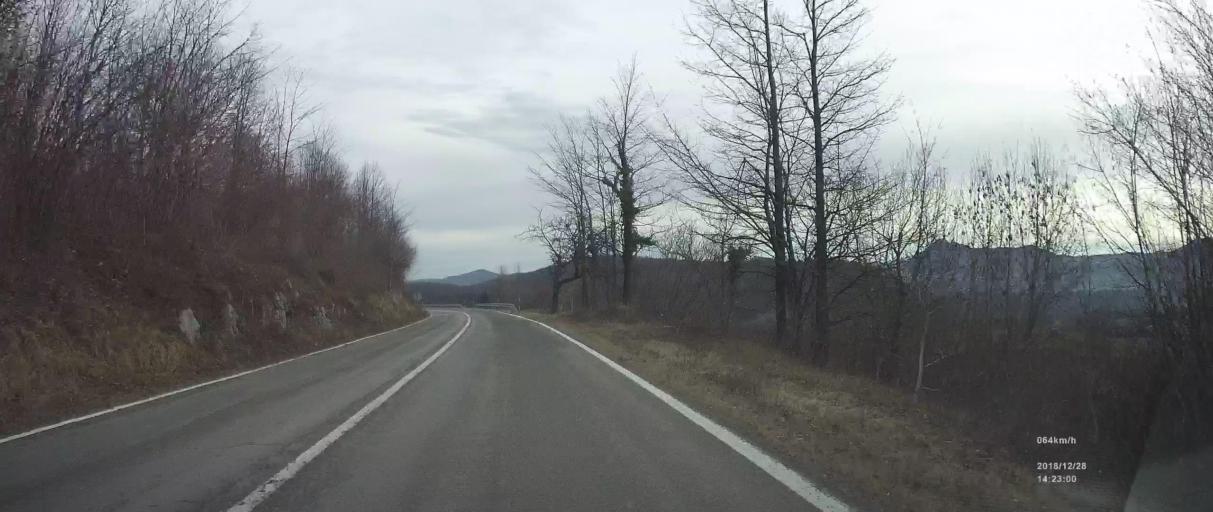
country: HR
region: Primorsko-Goranska
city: Vrbovsko
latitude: 45.3809
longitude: 15.0901
